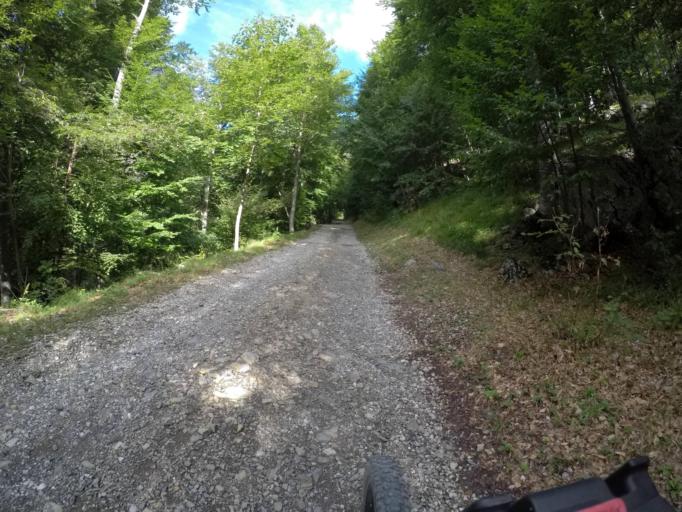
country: IT
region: Friuli Venezia Giulia
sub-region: Provincia di Udine
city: Paularo
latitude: 46.4867
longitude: 13.1816
